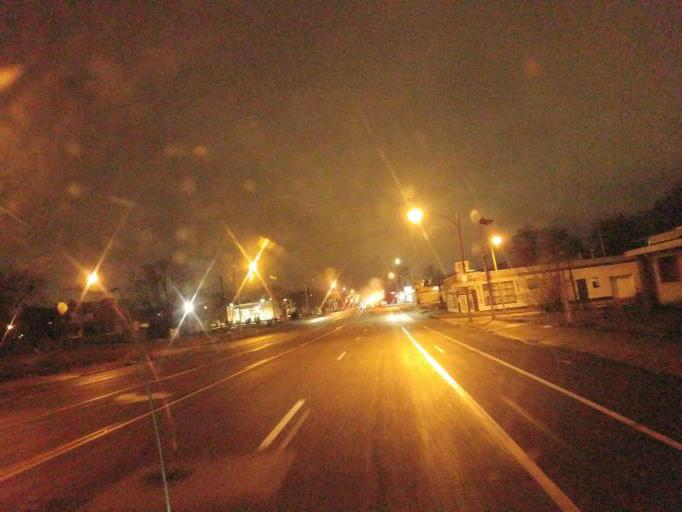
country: US
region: Missouri
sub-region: City of Saint Louis
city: St. Louis
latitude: 38.6486
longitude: -90.1989
